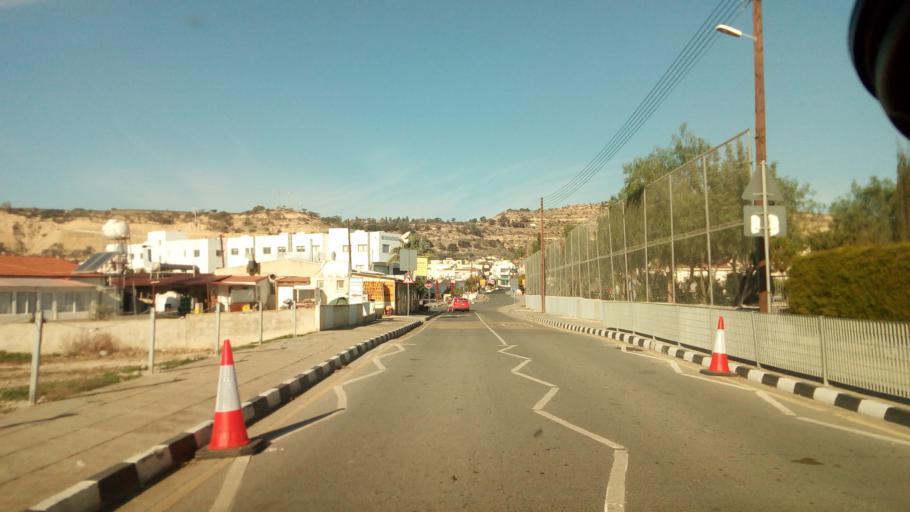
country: CY
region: Larnaka
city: Voroklini
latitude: 34.9825
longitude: 33.6567
